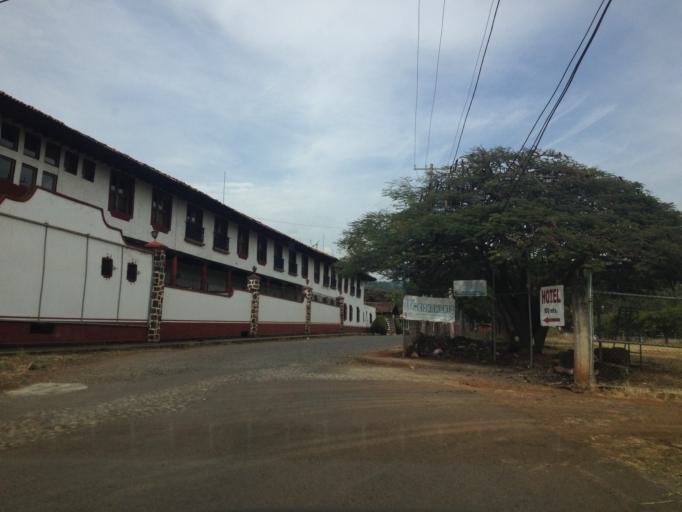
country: MX
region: Michoacan
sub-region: Ziracuaretiro
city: Patuan
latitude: 19.4303
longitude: -101.9241
